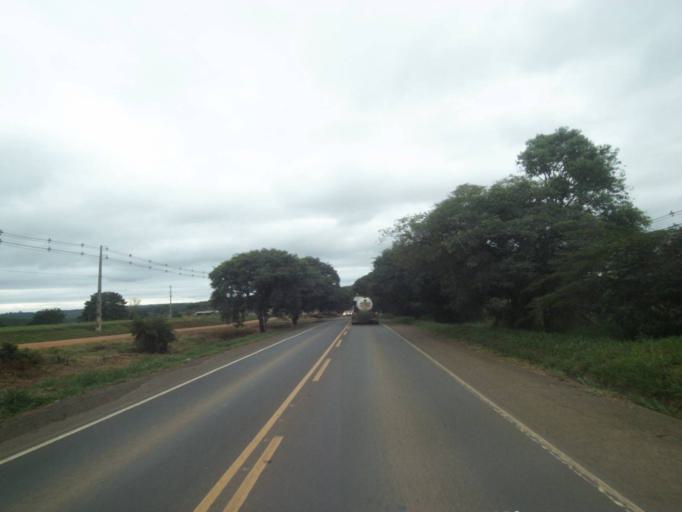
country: BR
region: Parana
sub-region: Telemaco Borba
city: Telemaco Borba
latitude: -24.3492
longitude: -50.6610
